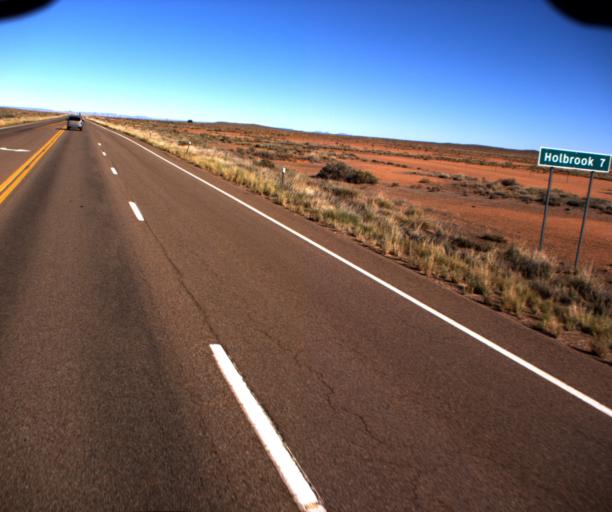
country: US
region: Arizona
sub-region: Navajo County
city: Holbrook
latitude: 34.7982
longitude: -110.1347
